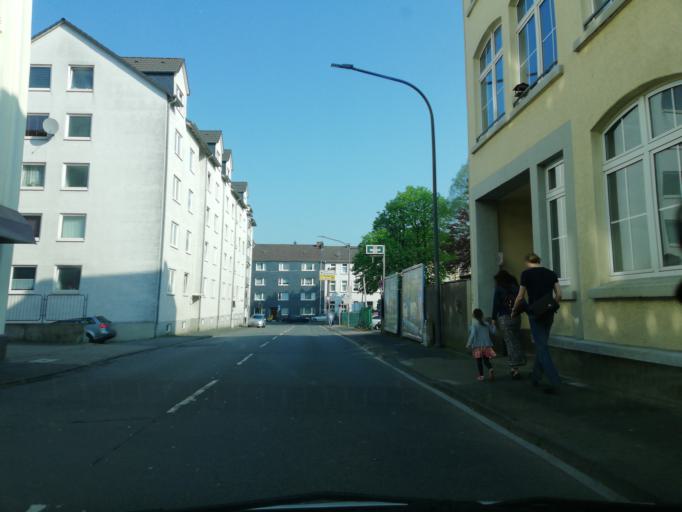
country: DE
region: North Rhine-Westphalia
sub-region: Regierungsbezirk Arnsberg
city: Schwelm
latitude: 51.2729
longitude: 7.2372
